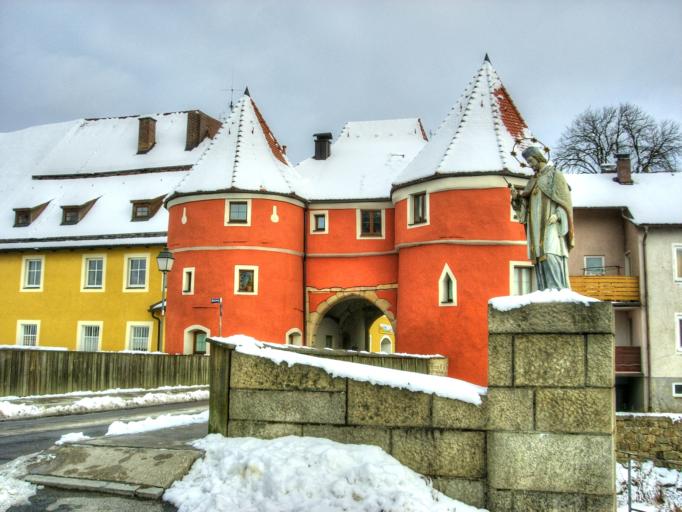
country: DE
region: Bavaria
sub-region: Upper Palatinate
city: Cham
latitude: 49.2186
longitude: 12.6616
